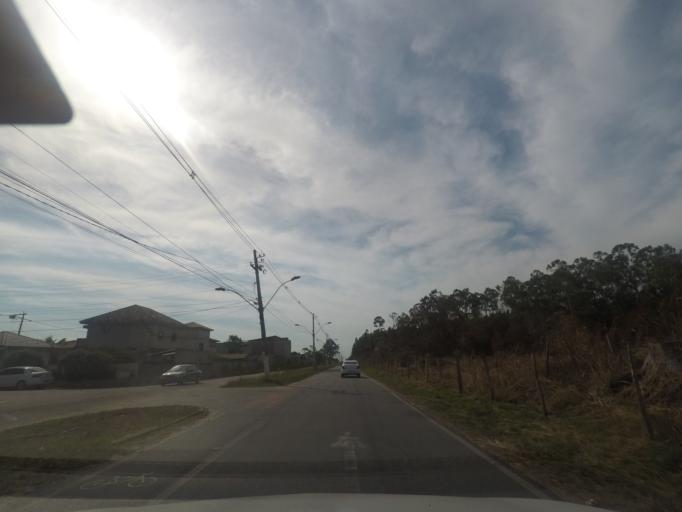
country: BR
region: Rio de Janeiro
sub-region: Marica
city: Marica
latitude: -22.9411
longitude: -42.8945
